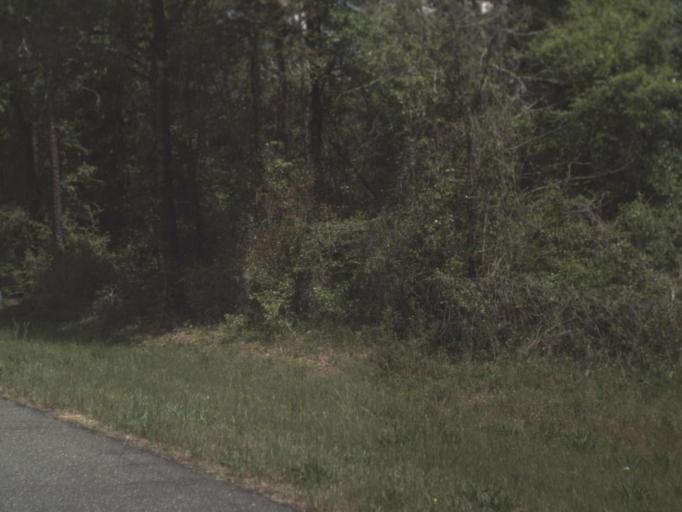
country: US
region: Florida
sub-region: Santa Rosa County
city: Point Baker
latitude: 30.7177
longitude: -87.0453
